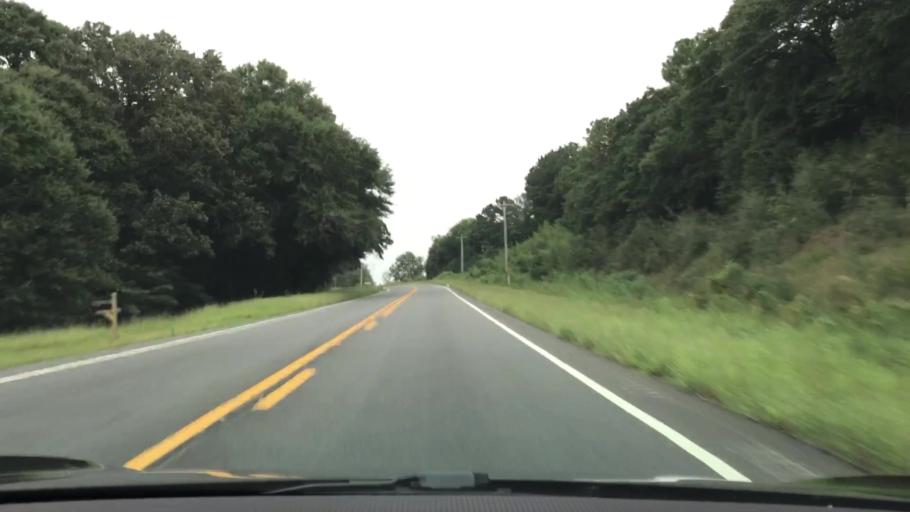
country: US
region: Alabama
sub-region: Covington County
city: Opp
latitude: 31.2294
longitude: -86.1620
